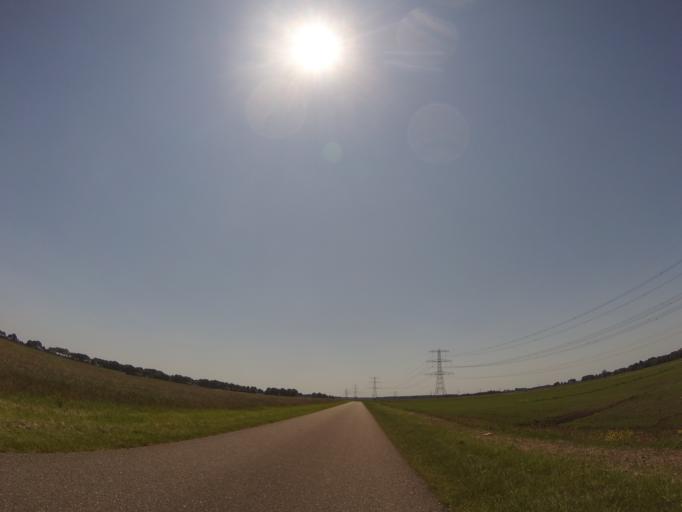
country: NL
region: Drenthe
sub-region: Gemeente Coevorden
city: Sleen
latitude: 52.7482
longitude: 6.8424
